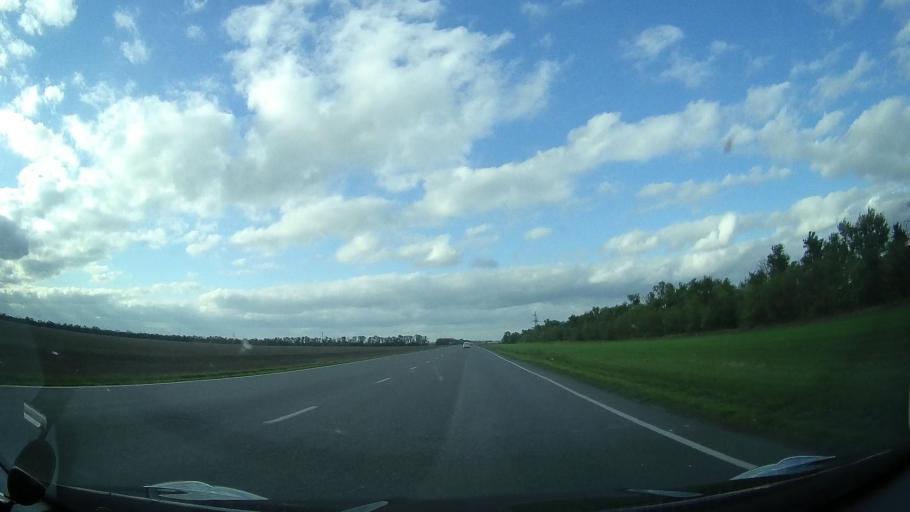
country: RU
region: Rostov
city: Kagal'nitskaya
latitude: 46.9244
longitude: 40.1014
